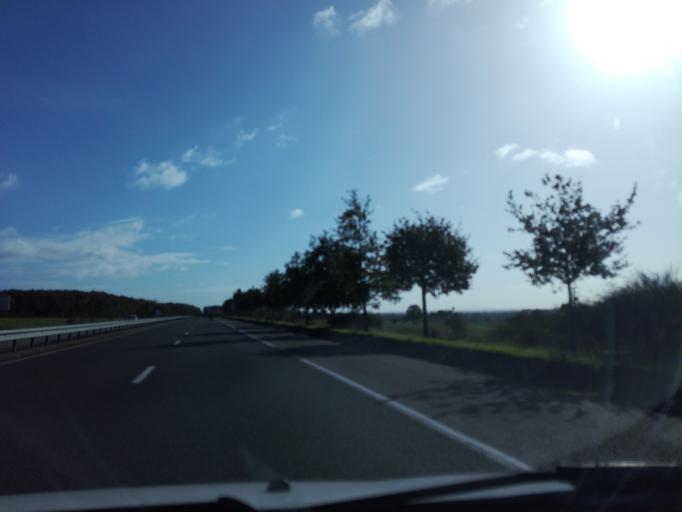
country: FR
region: Pays de la Loire
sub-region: Departement de Maine-et-Loire
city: Combree
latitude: 47.7171
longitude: -1.0214
